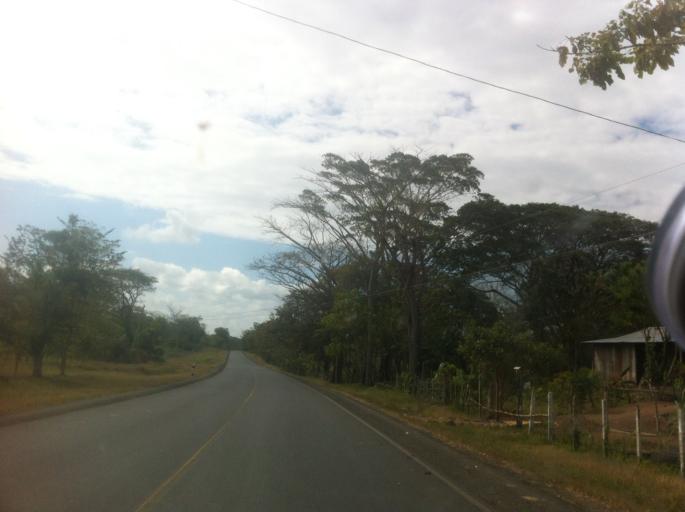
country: NI
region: Rio San Juan
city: San Carlos
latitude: 11.2997
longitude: -84.7277
